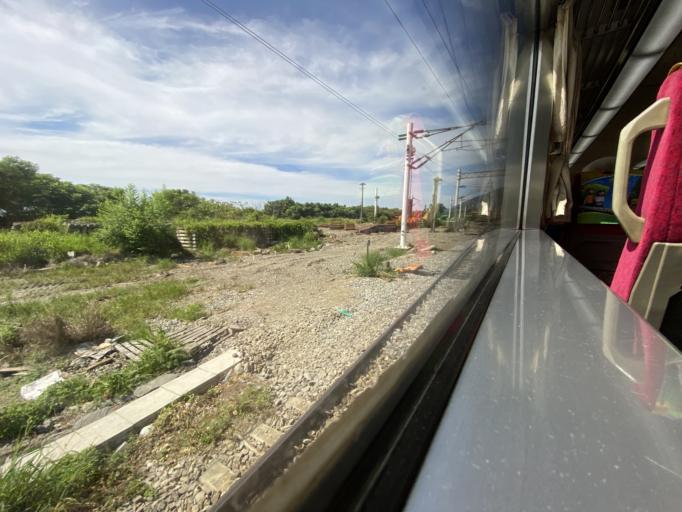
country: TW
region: Taiwan
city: Taitung City
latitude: 22.6211
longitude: 121.0065
